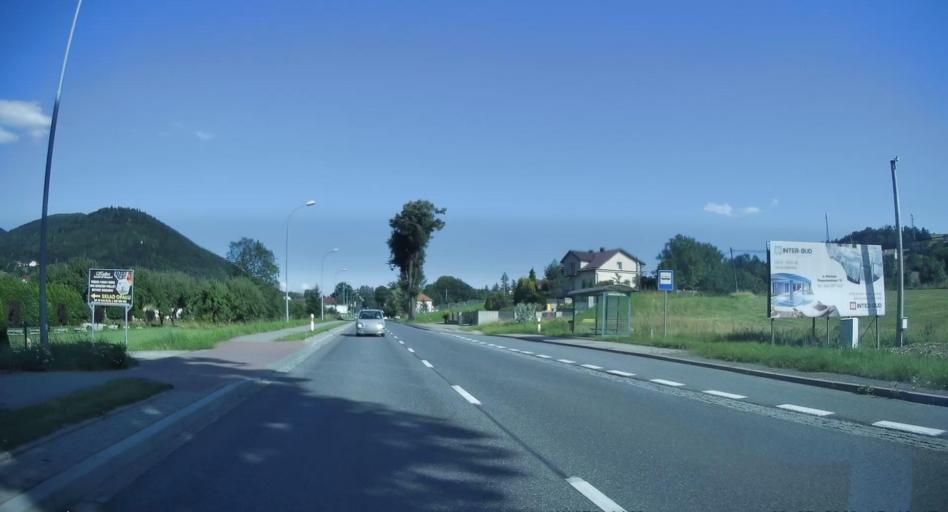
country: PL
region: Lesser Poland Voivodeship
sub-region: Powiat nowosadecki
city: Nawojowa
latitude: 49.5531
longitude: 20.7606
